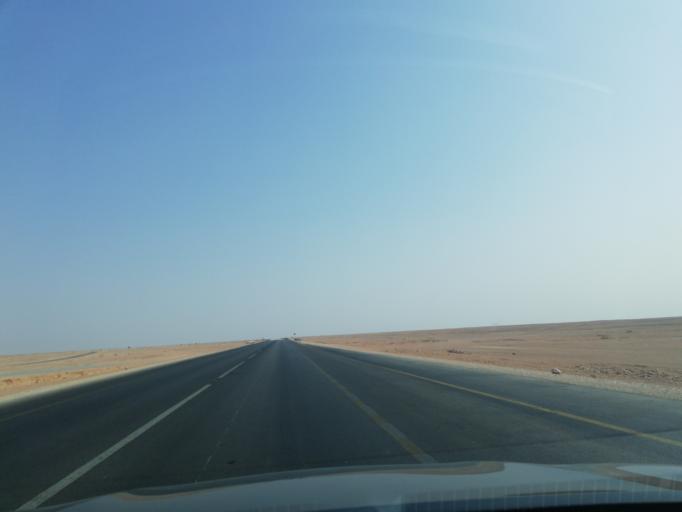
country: OM
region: Zufar
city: Salalah
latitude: 17.8183
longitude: 54.0008
